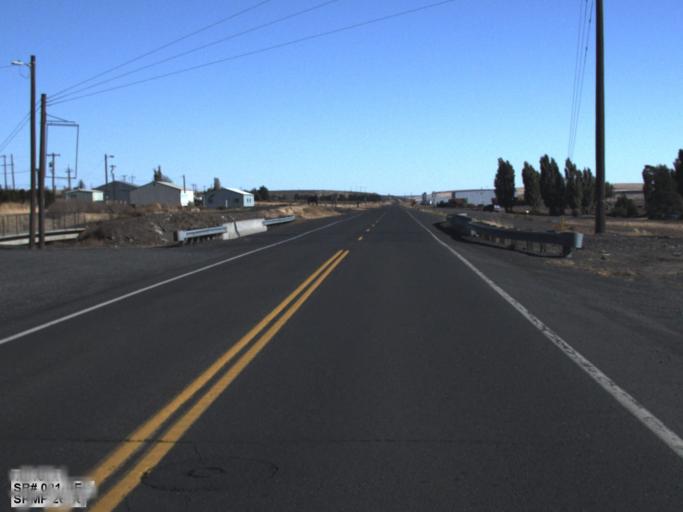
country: US
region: Washington
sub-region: Adams County
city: Ritzville
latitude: 46.9716
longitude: -118.6110
